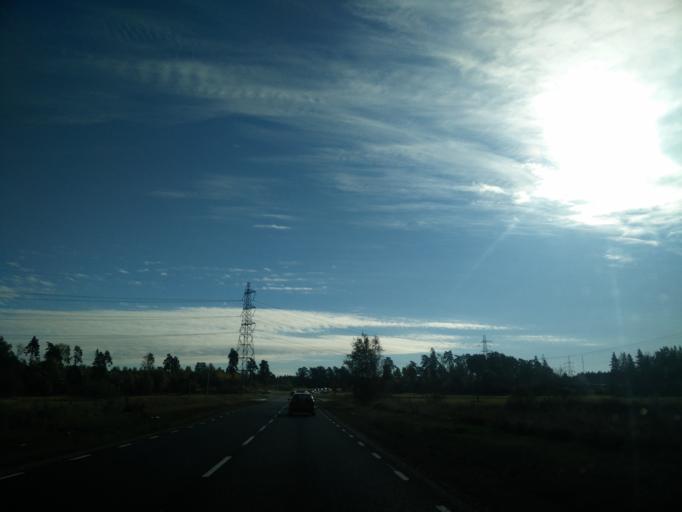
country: SE
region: Stockholm
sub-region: Upplands Vasby Kommun
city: Upplands Vaesby
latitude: 59.5071
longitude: 17.9693
